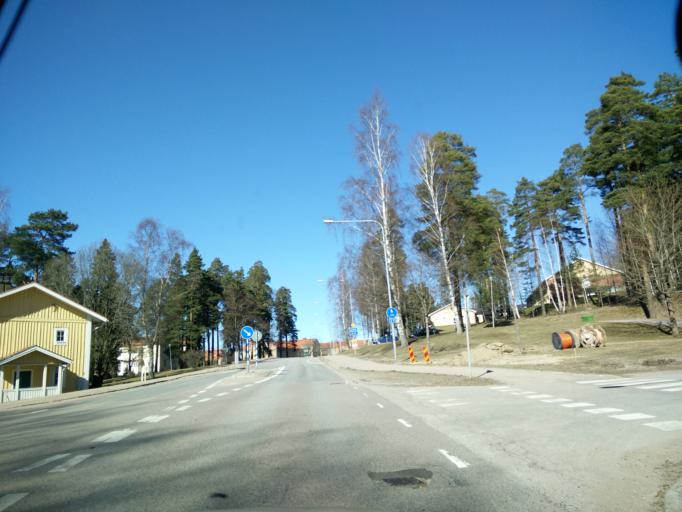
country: SE
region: Vaermland
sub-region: Hagfors Kommun
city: Hagfors
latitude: 60.0278
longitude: 13.6993
